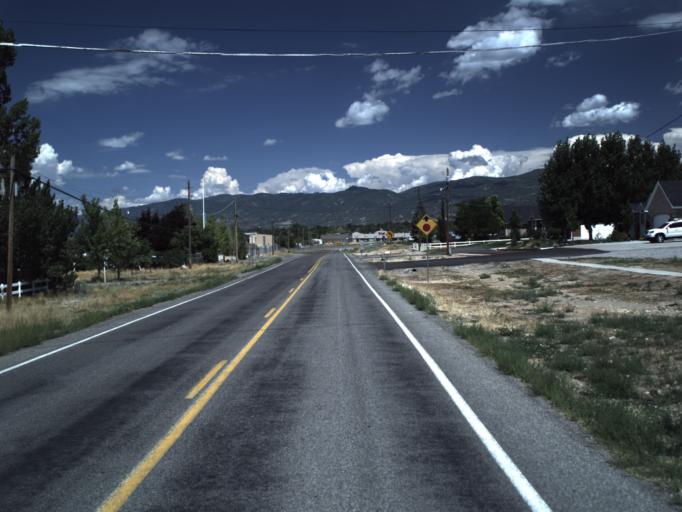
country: US
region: Utah
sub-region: Sanpete County
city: Mount Pleasant
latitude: 39.5266
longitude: -111.4688
